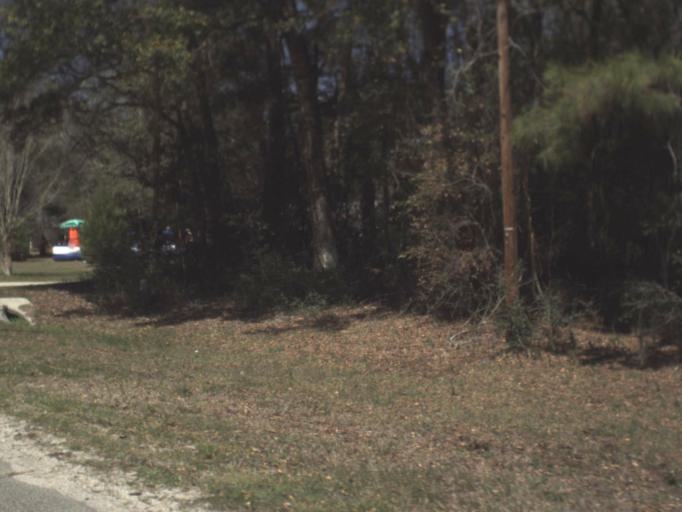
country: US
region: Florida
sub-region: Leon County
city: Woodville
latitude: 30.2286
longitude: -84.2202
